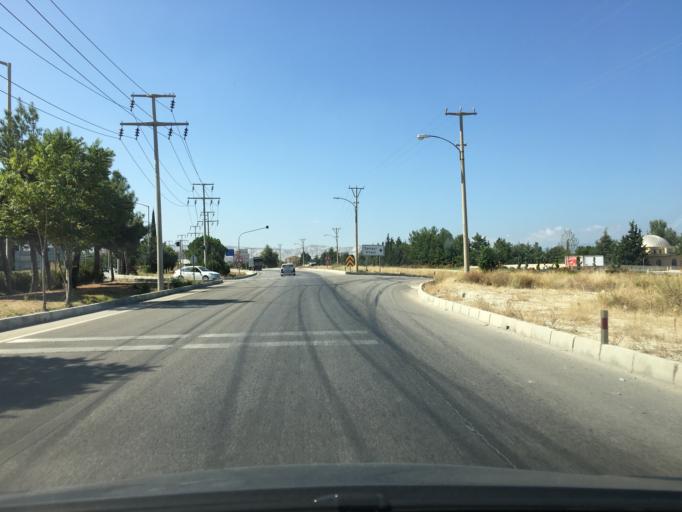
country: TR
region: Burdur
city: Burdur
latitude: 37.7432
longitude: 30.3148
